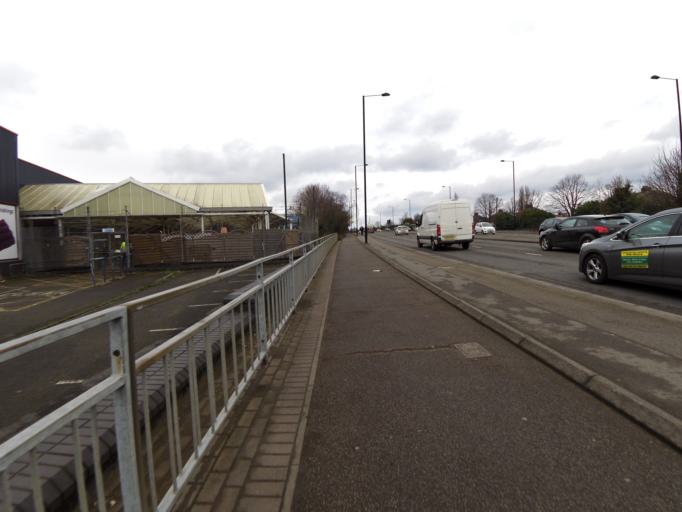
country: GB
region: England
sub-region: Doncaster
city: Bentley
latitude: 53.5331
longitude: -1.1561
